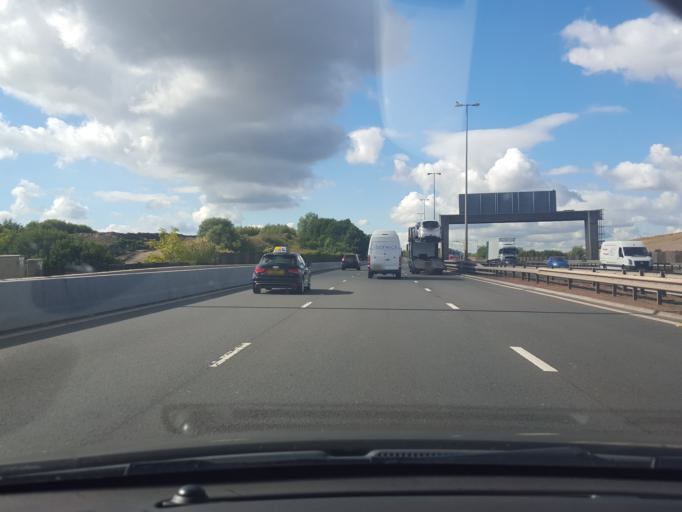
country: GB
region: Scotland
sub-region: South Lanarkshire
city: Uddingston
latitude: 55.8348
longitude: -4.1293
